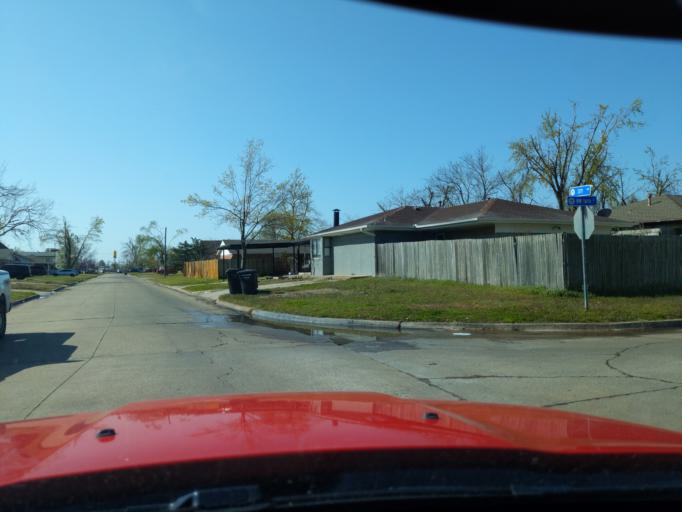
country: US
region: Oklahoma
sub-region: Cleveland County
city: Moore
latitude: 35.3521
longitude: -97.4989
